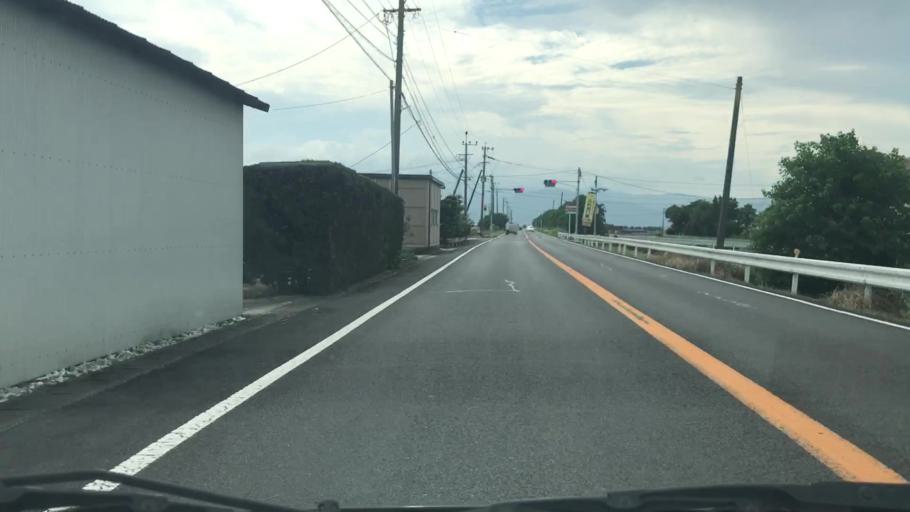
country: JP
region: Saga Prefecture
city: Kashima
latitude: 33.1445
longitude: 130.1470
